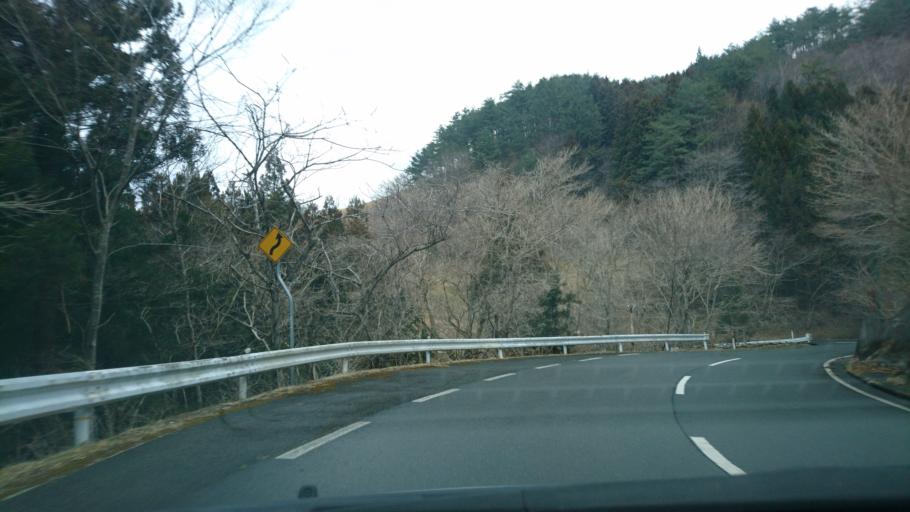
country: JP
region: Iwate
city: Ofunato
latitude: 38.9996
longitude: 141.5473
